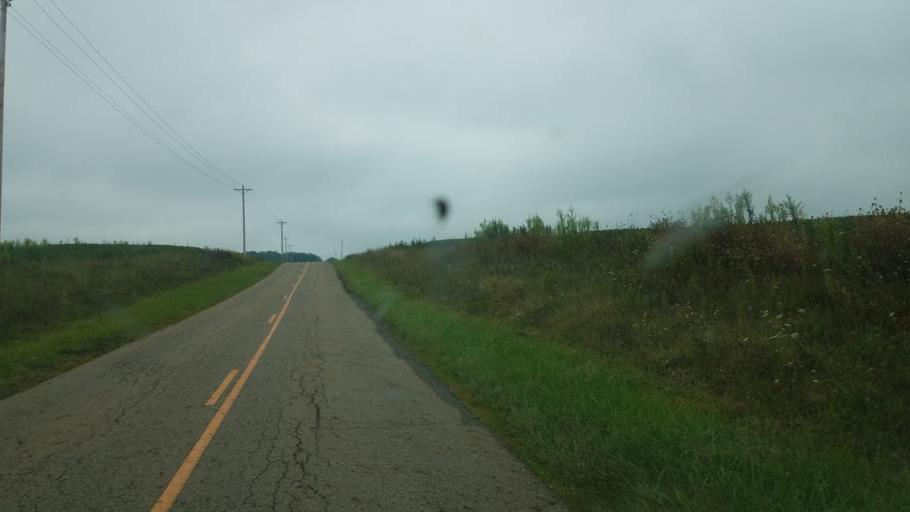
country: US
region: Ohio
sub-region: Licking County
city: Utica
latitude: 40.2930
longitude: -82.4320
